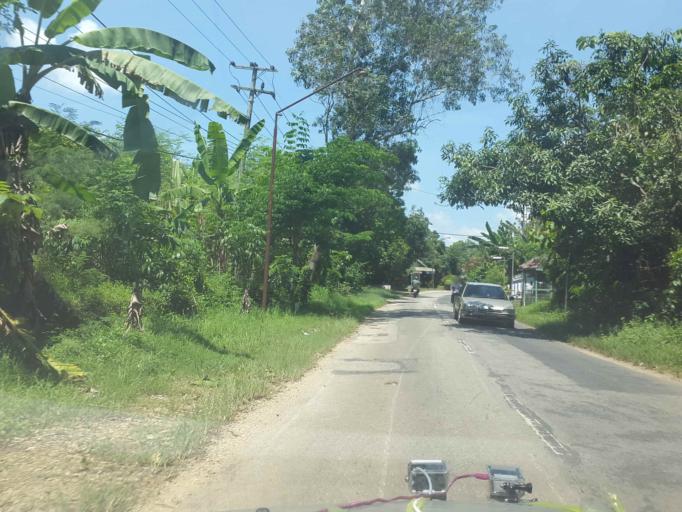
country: ID
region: East Java
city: Ganjur
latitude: -6.9852
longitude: 113.8600
